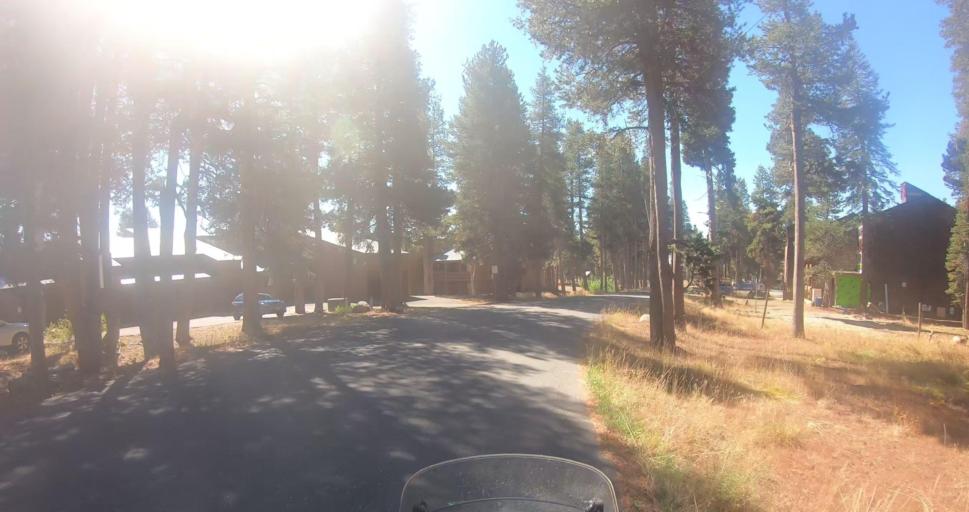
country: US
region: California
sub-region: Calaveras County
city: Arnold
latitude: 38.4639
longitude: -120.0404
